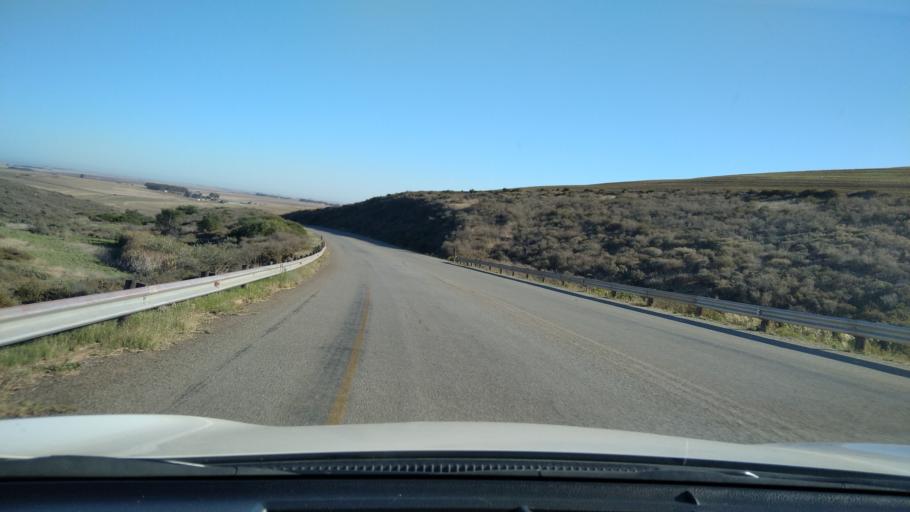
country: ZA
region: Western Cape
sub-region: West Coast District Municipality
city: Malmesbury
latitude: -33.3832
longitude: 18.6697
